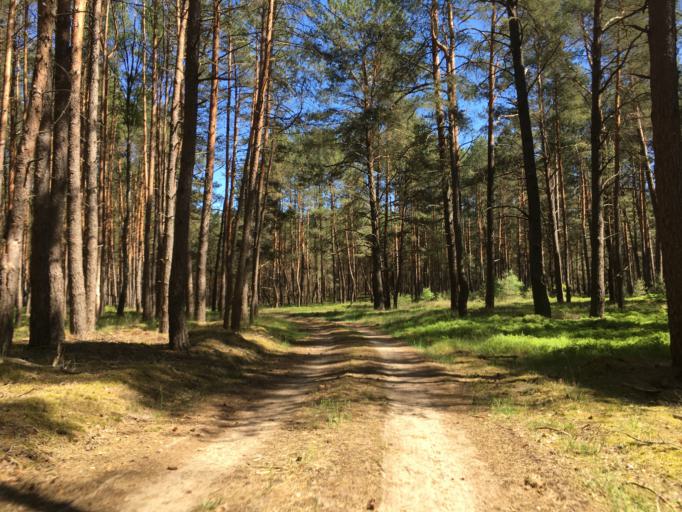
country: DE
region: Brandenburg
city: Friedrichswalde
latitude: 52.9659
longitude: 13.6498
